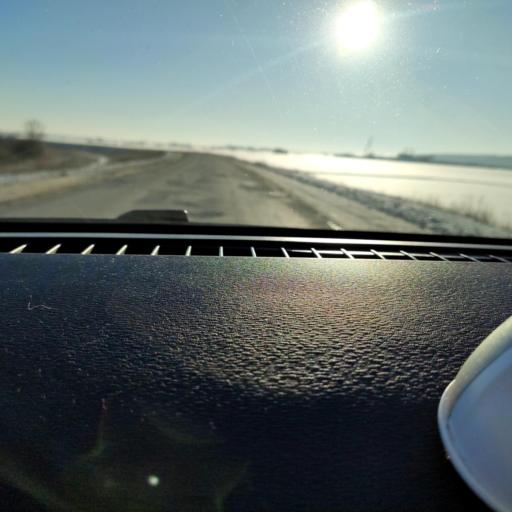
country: RU
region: Samara
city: Spiridonovka
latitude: 53.1372
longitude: 50.6020
